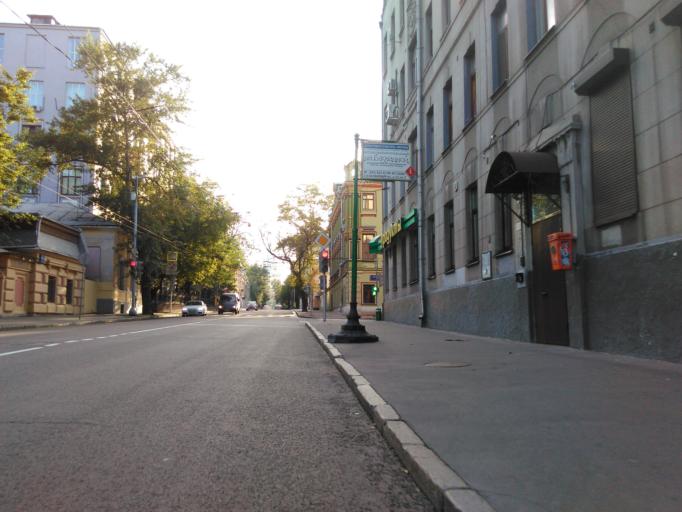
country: RU
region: Moscow
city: Sokol'niki
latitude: 55.7698
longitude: 37.6637
